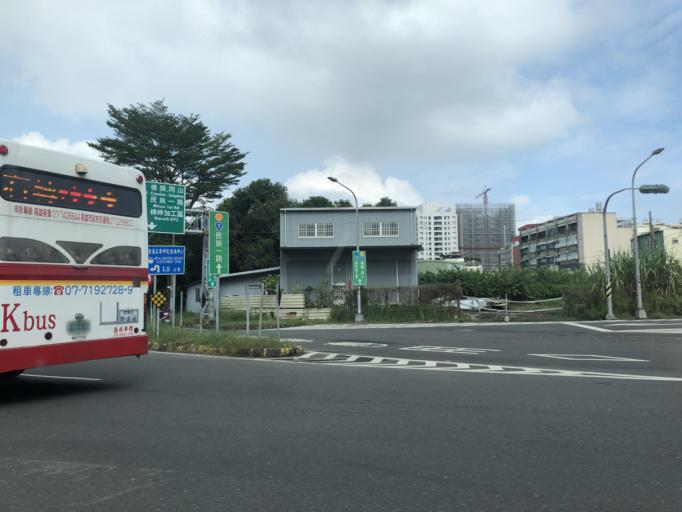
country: TW
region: Taiwan
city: Fengshan
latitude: 22.7227
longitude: 120.3273
